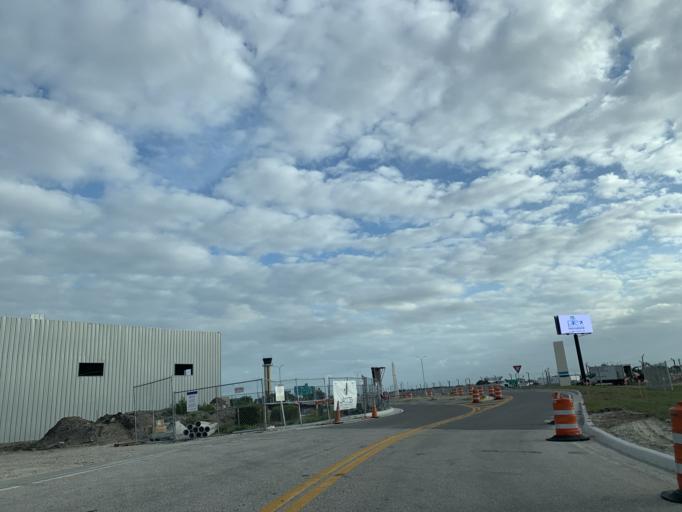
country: US
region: Florida
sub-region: Pinellas County
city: South Highpoint
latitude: 27.9074
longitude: -82.6958
